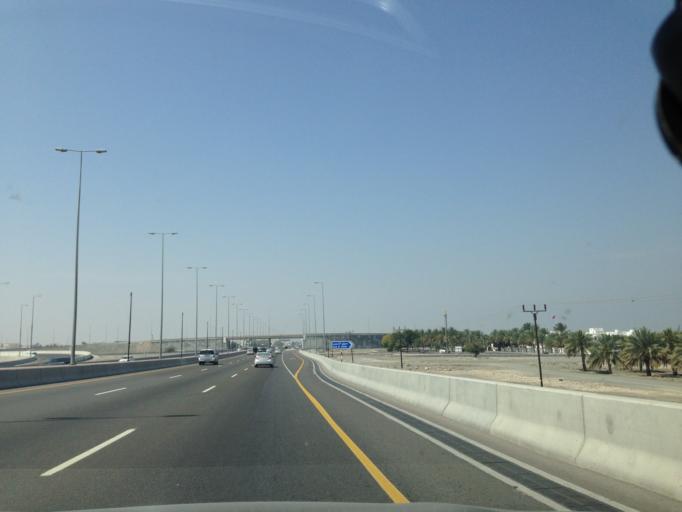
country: OM
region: Muhafazat Masqat
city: As Sib al Jadidah
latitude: 23.6644
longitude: 58.1651
